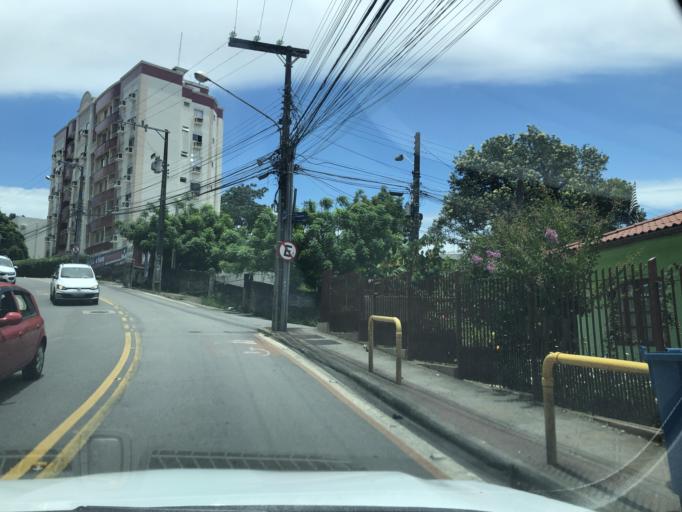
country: BR
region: Santa Catarina
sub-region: Florianopolis
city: Itacorubi
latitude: -27.5858
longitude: -48.4972
